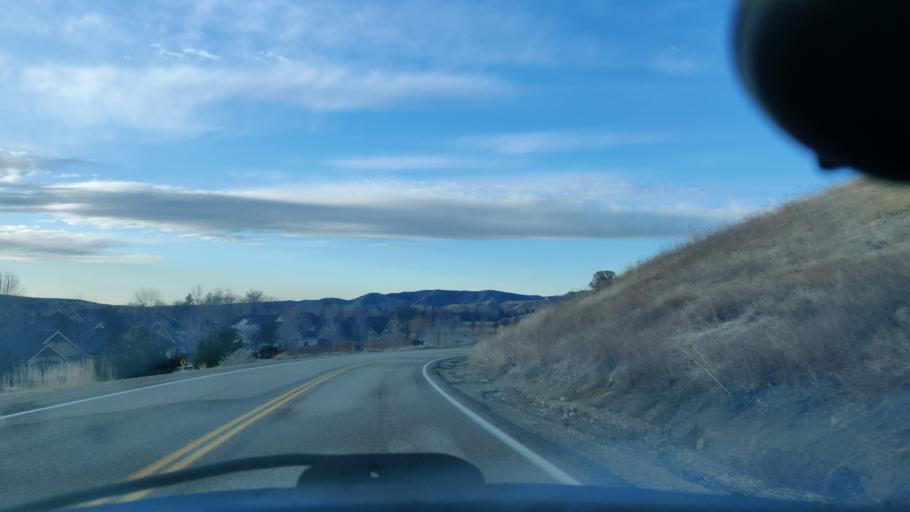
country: US
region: Idaho
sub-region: Ada County
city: Garden City
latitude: 43.7218
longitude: -116.2422
